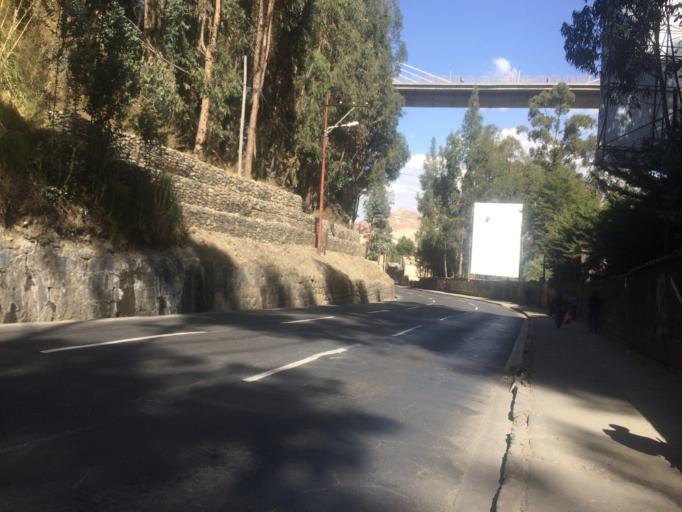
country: BO
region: La Paz
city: La Paz
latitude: -16.5148
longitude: -68.1177
